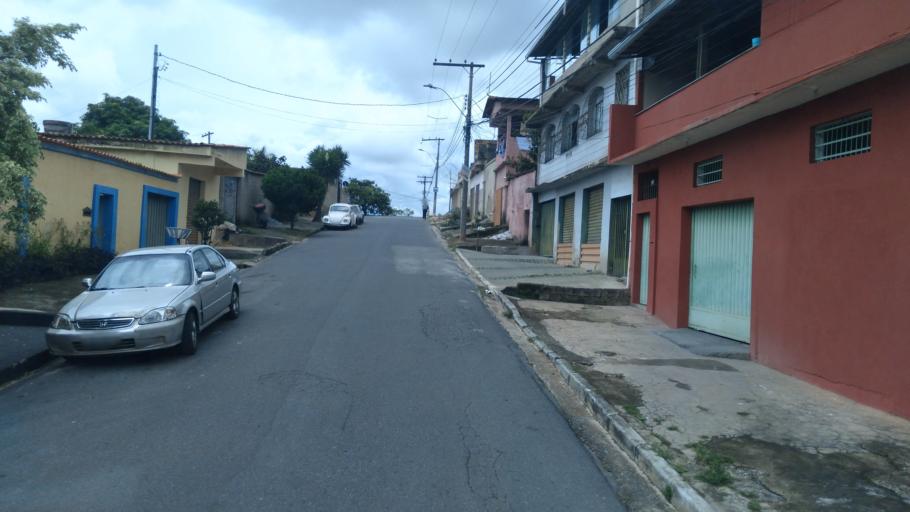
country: BR
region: Minas Gerais
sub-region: Belo Horizonte
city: Belo Horizonte
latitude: -19.9162
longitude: -43.8861
